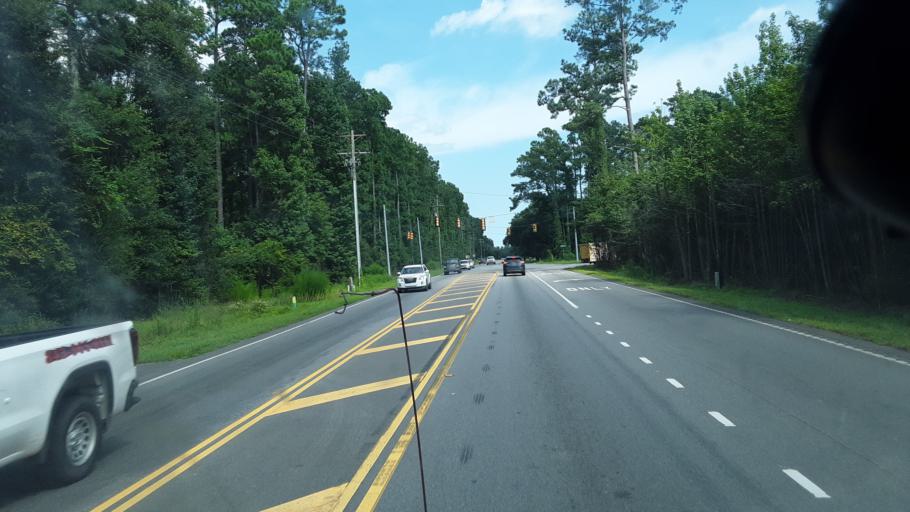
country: US
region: South Carolina
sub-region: Horry County
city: Red Hill
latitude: 33.8221
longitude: -78.9156
